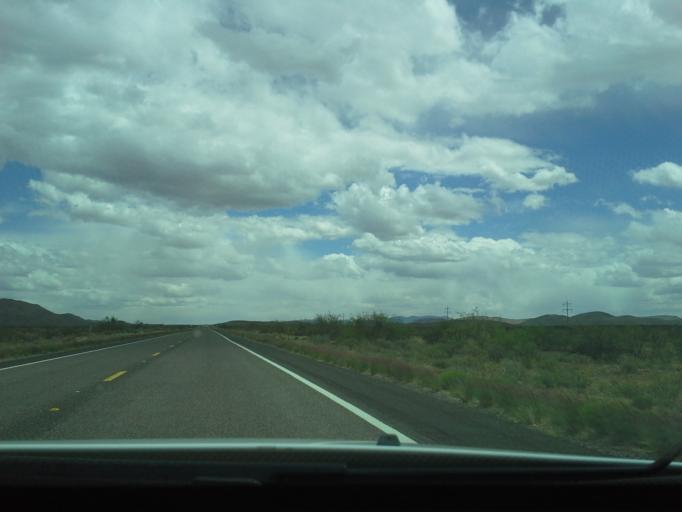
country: US
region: Arizona
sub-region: Graham County
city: Swift Trail Junction
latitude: 32.7637
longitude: -109.4498
